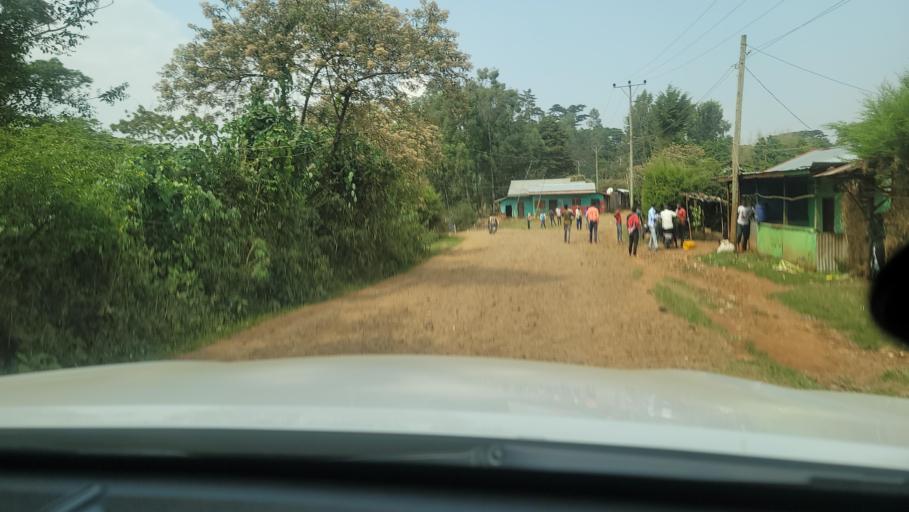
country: ET
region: Oromiya
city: Agaro
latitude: 7.8057
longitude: 36.4660
